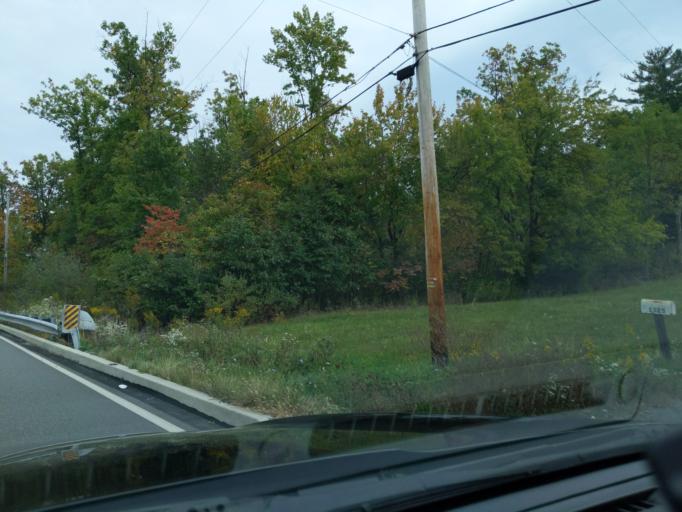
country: US
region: Pennsylvania
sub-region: Blair County
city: Lakemont
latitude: 40.4817
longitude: -78.3915
